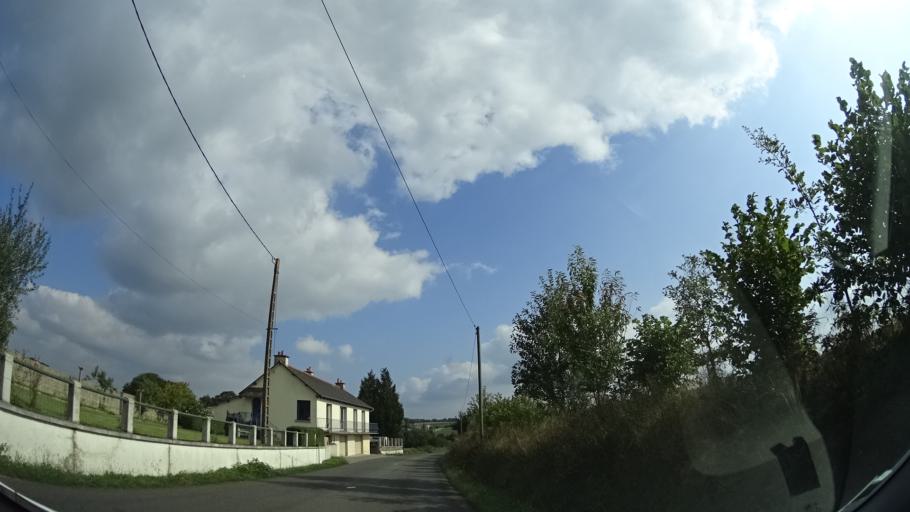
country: FR
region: Brittany
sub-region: Departement d'Ille-et-Vilaine
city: Pleumeleuc
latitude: 48.1967
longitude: -1.9080
